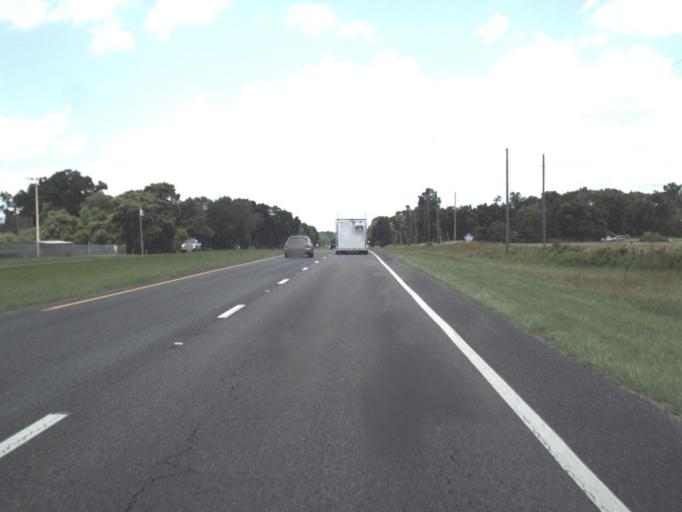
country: US
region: Florida
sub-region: Alachua County
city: High Springs
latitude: 29.8140
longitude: -82.5669
